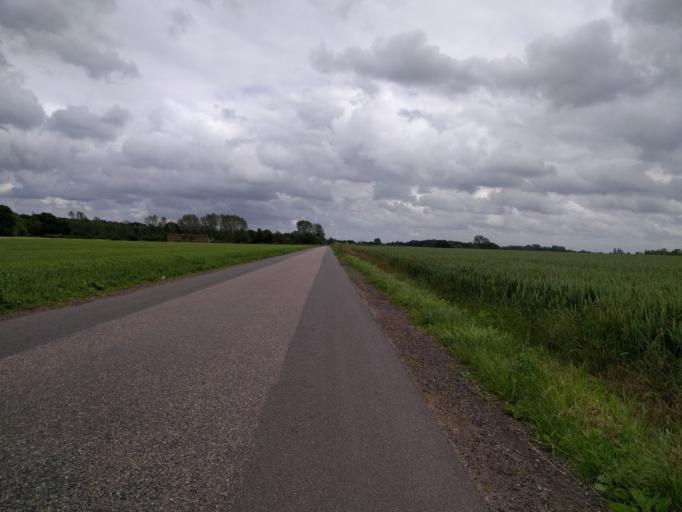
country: DK
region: South Denmark
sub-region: Odense Kommune
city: Bullerup
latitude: 55.4311
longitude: 10.5159
